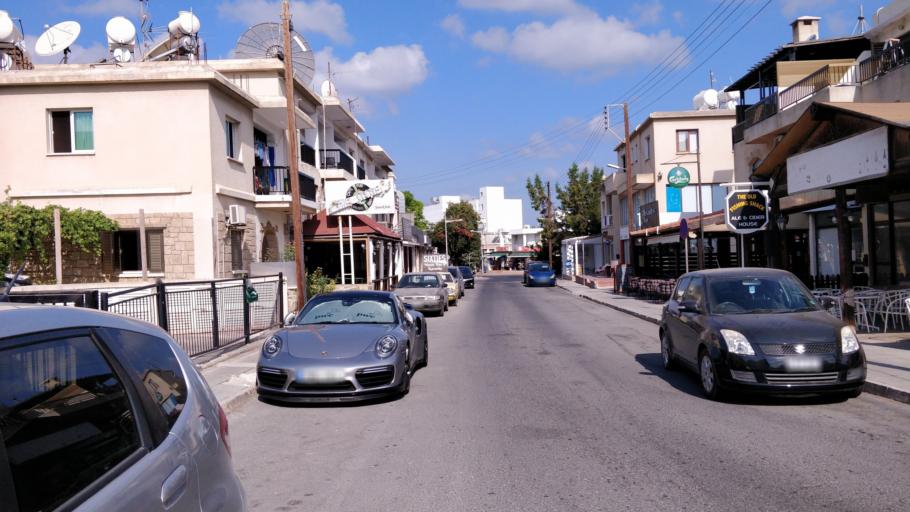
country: CY
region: Pafos
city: Paphos
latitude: 34.7583
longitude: 32.4177
